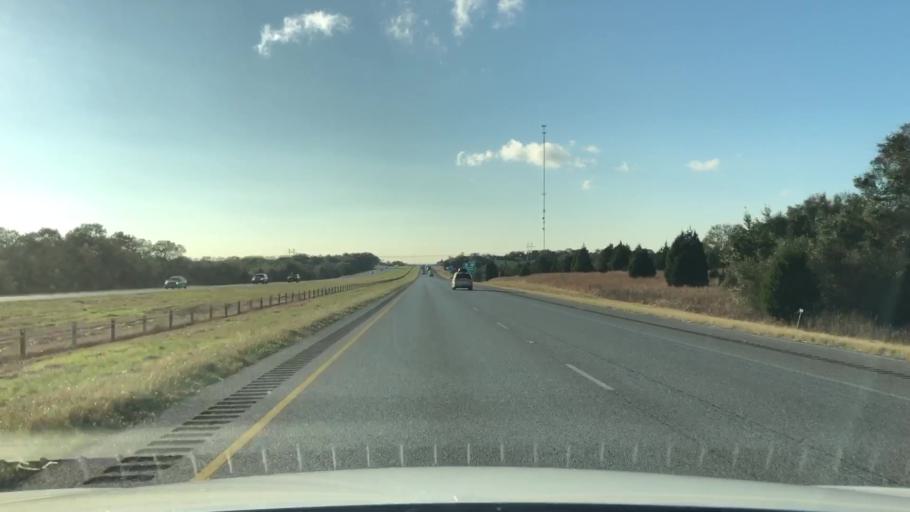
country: US
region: Texas
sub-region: Fayette County
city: Flatonia
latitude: 29.6975
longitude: -97.0788
